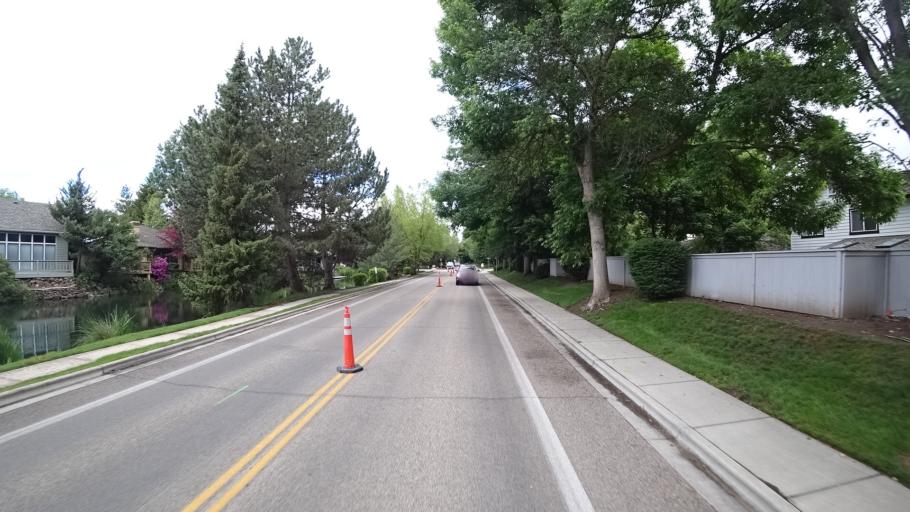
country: US
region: Idaho
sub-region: Ada County
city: Garden City
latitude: 43.6655
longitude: -116.2908
